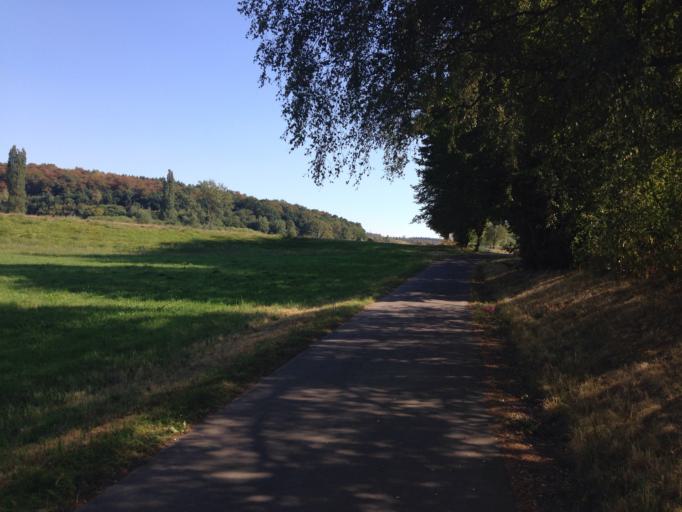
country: DE
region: Hesse
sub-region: Regierungsbezirk Giessen
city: Rabenau
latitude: 50.6566
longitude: 8.8921
